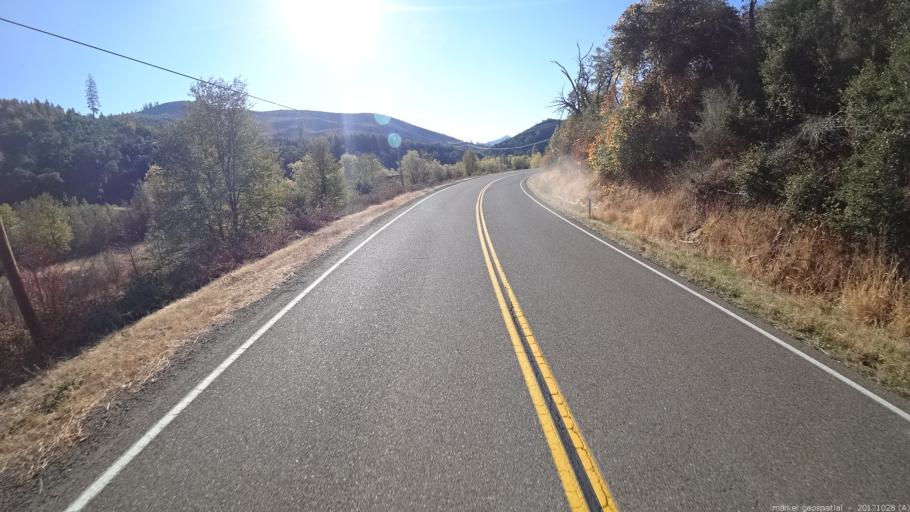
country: US
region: California
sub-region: Trinity County
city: Lewiston
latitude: 40.6846
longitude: -122.6391
